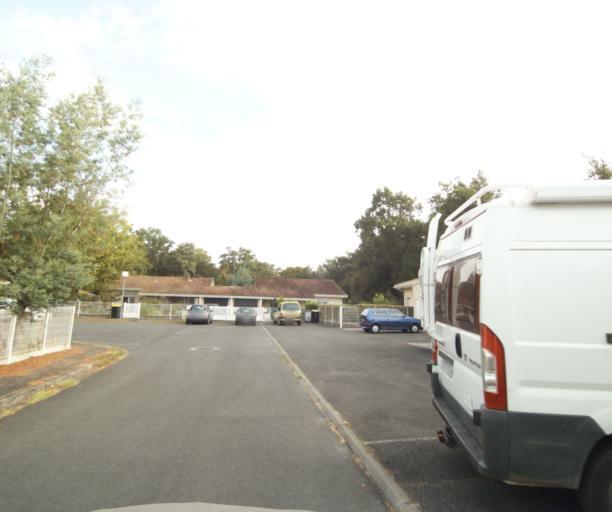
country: FR
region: Aquitaine
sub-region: Departement de la Gironde
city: Creon
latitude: 44.7813
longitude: -0.3549
